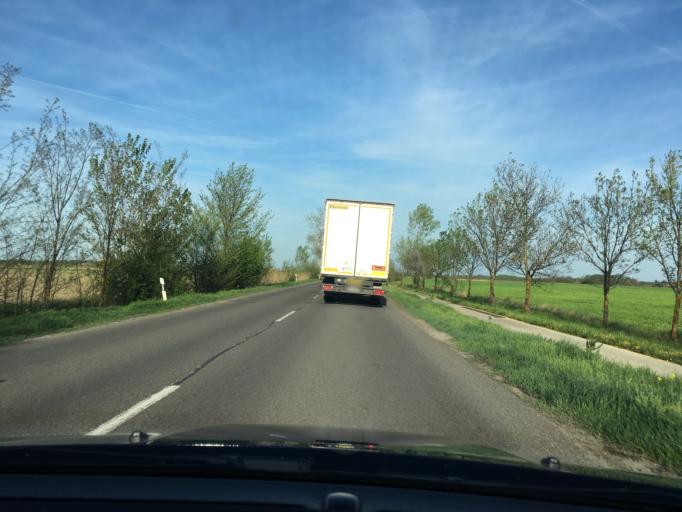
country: HU
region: Bekes
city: Korosladany
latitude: 47.0003
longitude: 21.1110
